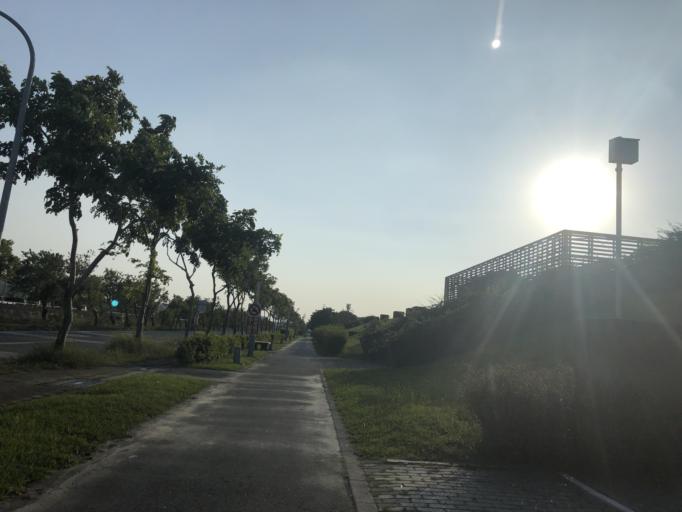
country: TW
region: Taiwan
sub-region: Tainan
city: Tainan
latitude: 23.0579
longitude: 120.2375
